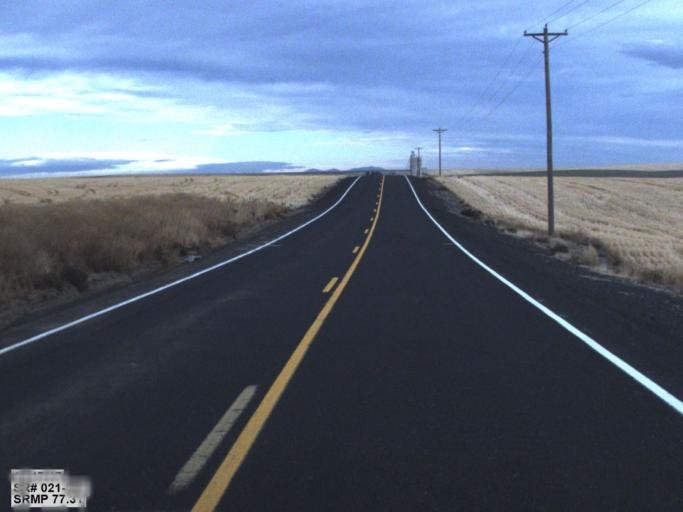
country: US
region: Washington
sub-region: Okanogan County
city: Coulee Dam
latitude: 47.6007
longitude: -118.7861
